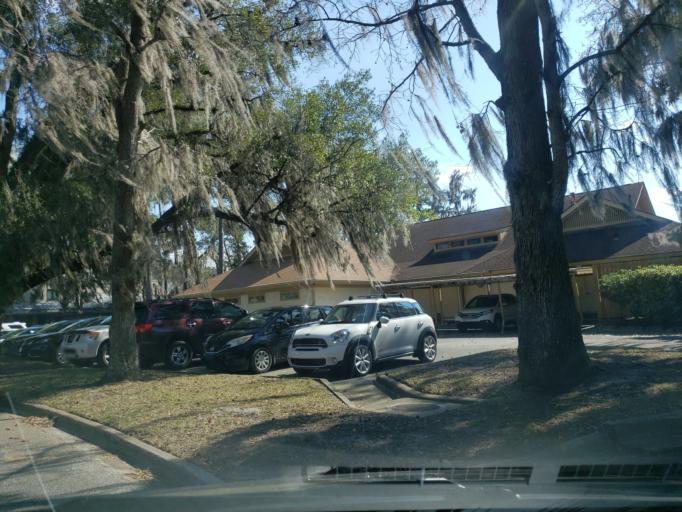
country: US
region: Georgia
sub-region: Chatham County
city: Isle of Hope
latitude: 32.0185
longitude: -81.1140
